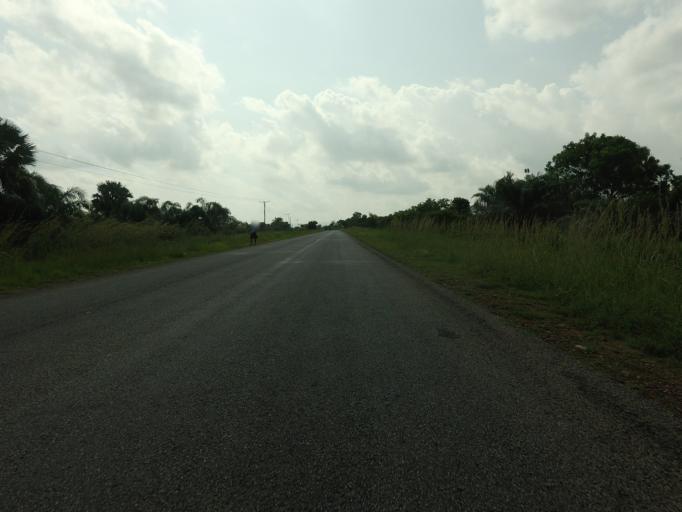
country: GH
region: Volta
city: Ho
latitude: 6.5836
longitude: 0.5743
